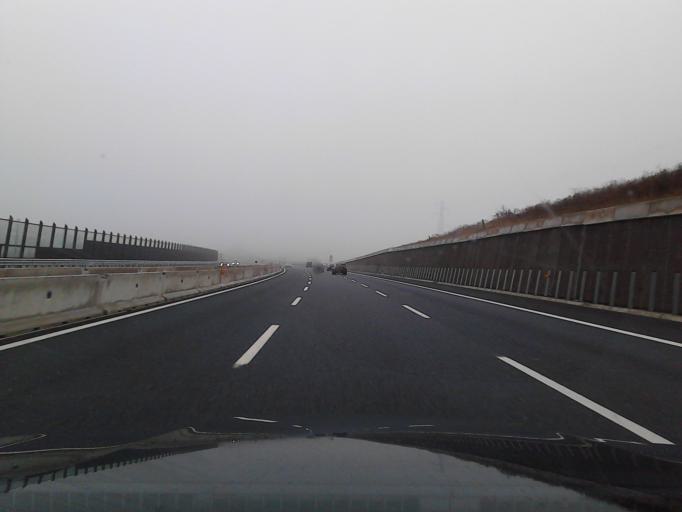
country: IT
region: The Marches
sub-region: Provincia di Pesaro e Urbino
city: Gradara
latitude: 43.9282
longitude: 12.7954
